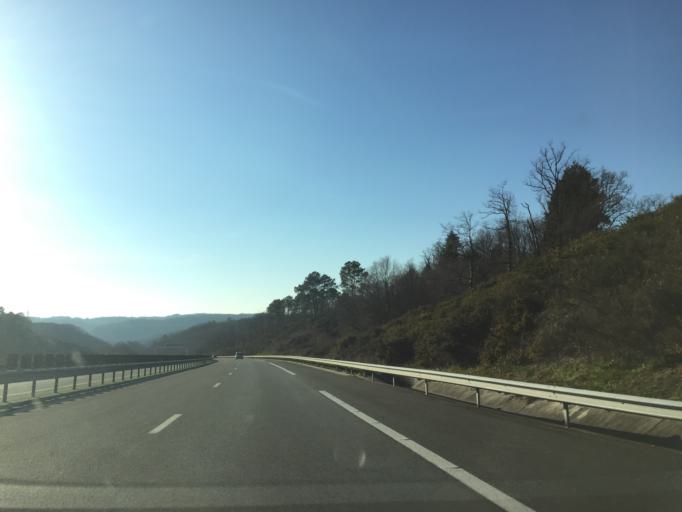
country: FR
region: Limousin
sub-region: Departement de la Correze
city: Cublac
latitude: 45.1632
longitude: 1.2261
